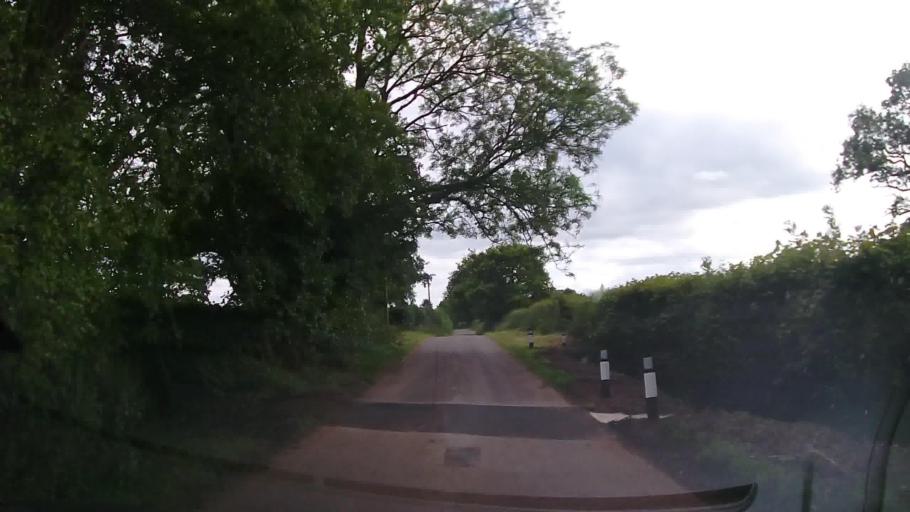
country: GB
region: England
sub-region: Shropshire
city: Whitchurch
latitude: 52.9266
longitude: -2.7241
